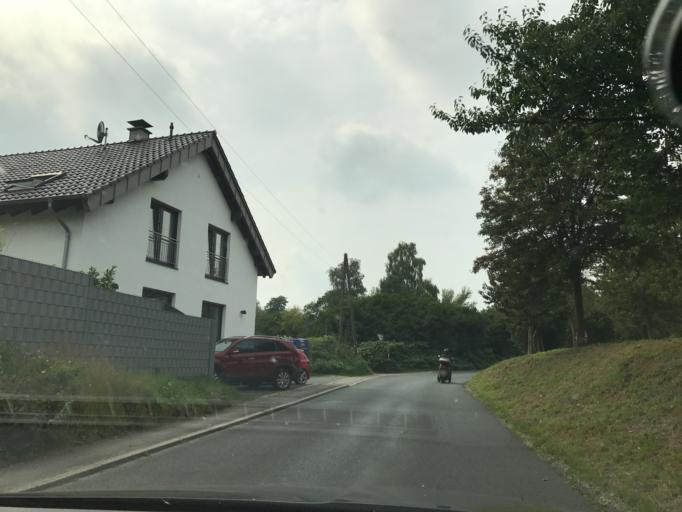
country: DE
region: North Rhine-Westphalia
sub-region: Regierungsbezirk Dusseldorf
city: Muelheim (Ruhr)
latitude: 51.4499
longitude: 6.9432
